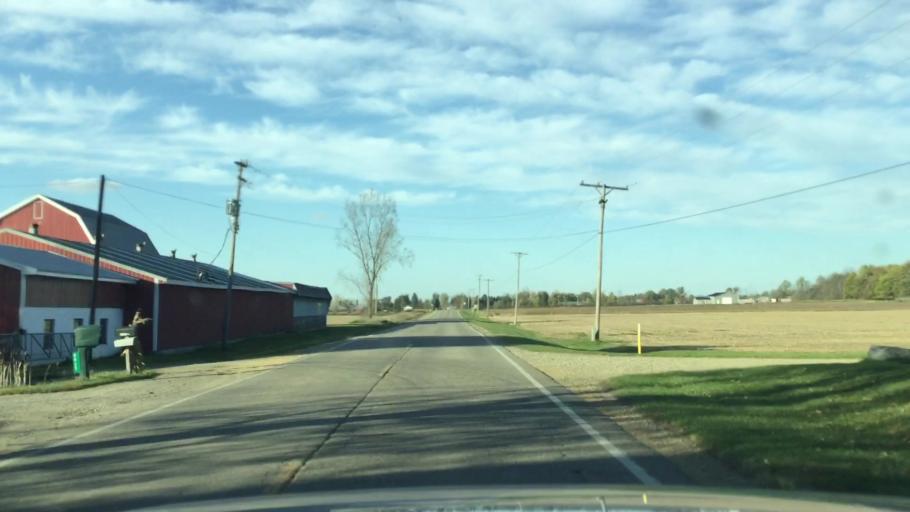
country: US
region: Michigan
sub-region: Lapeer County
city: North Branch
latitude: 43.2913
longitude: -83.1986
